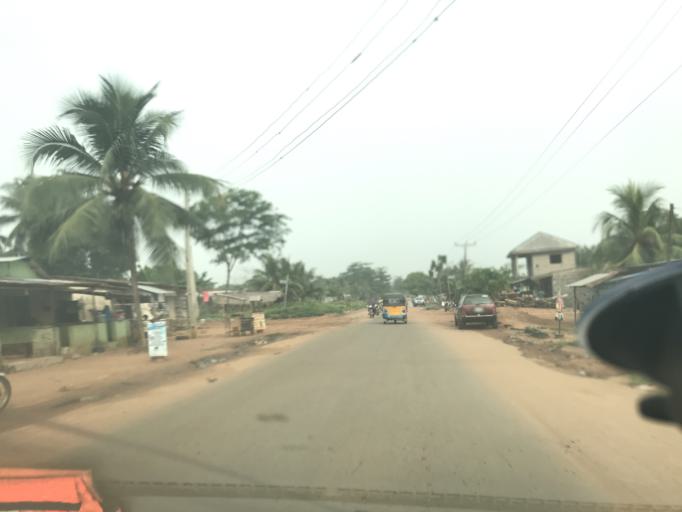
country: NG
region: Ogun
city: Ado Odo
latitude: 6.5009
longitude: 2.9540
